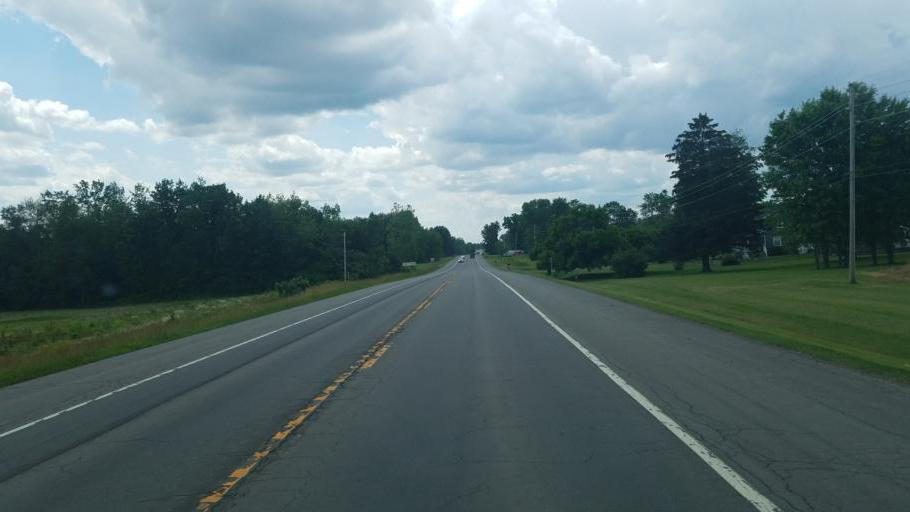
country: US
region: New York
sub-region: Seneca County
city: Waterloo
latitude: 42.9607
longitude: -76.8525
